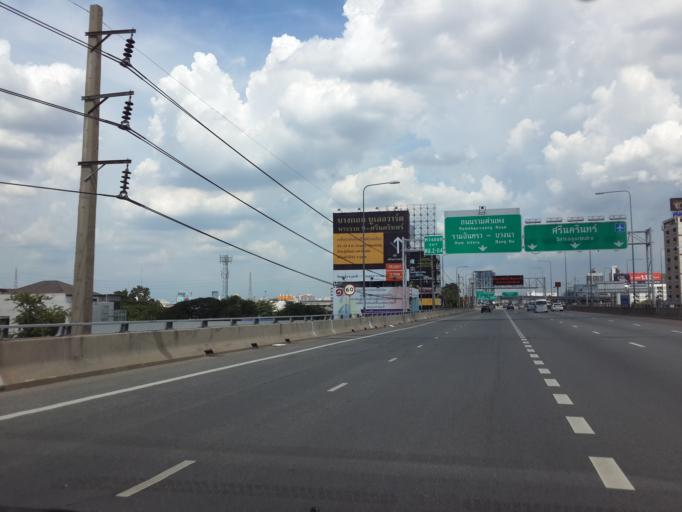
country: TH
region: Bangkok
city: Watthana
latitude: 13.7538
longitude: 100.5868
